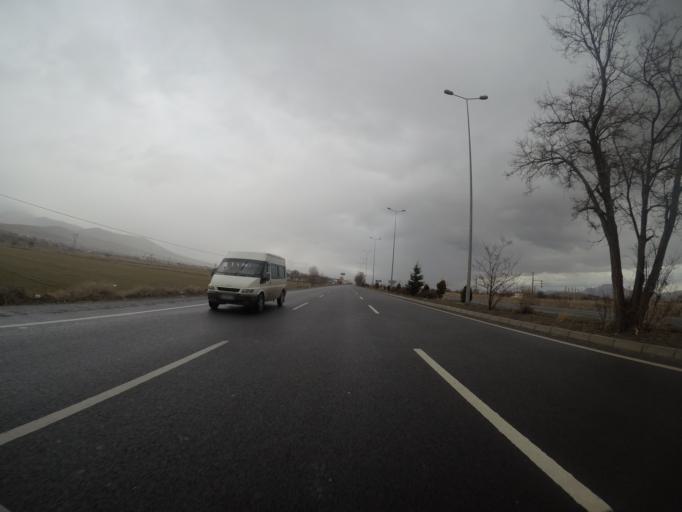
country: TR
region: Kayseri
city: Incesu
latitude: 38.6879
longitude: 35.2404
